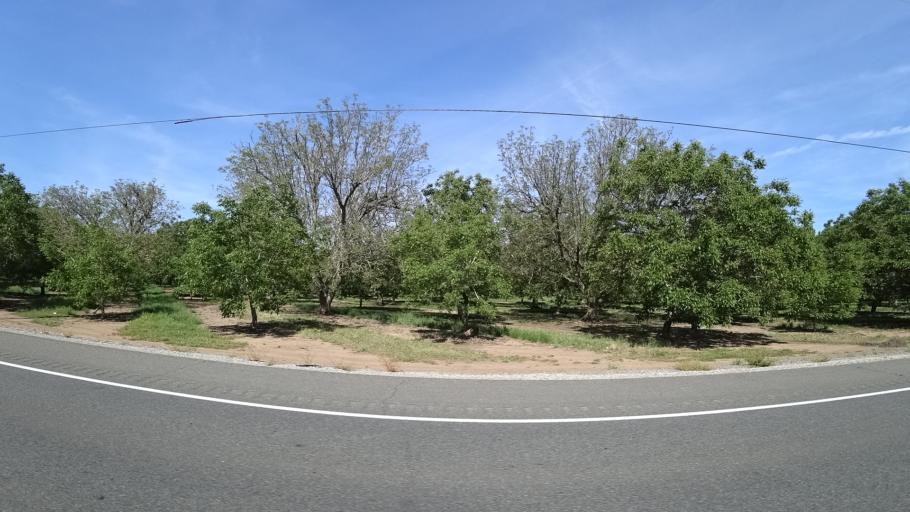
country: US
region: California
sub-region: Tehama County
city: Red Bluff
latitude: 40.1666
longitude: -122.1558
